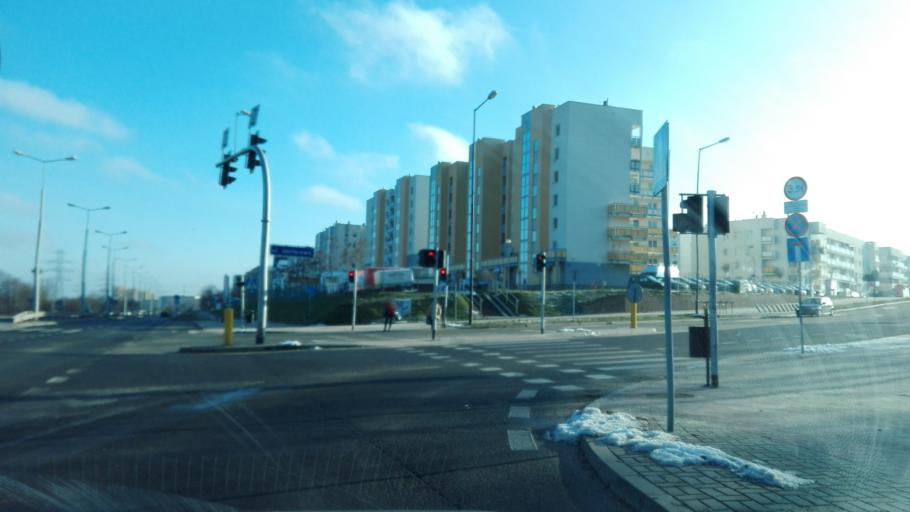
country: PL
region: Lublin Voivodeship
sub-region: Powiat lubelski
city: Kozubszczyzna
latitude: 51.2258
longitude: 22.4915
